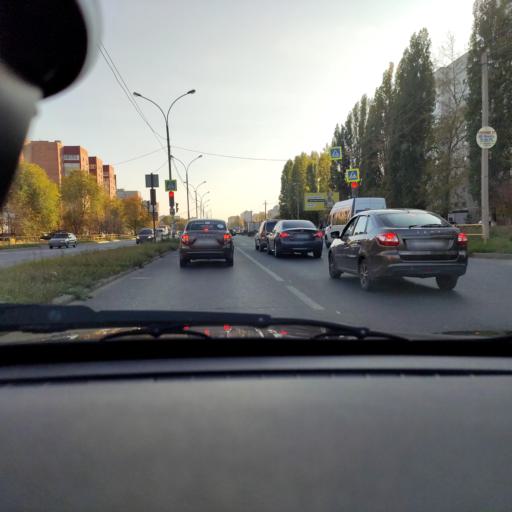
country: RU
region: Samara
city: Tol'yatti
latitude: 53.5401
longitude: 49.3152
